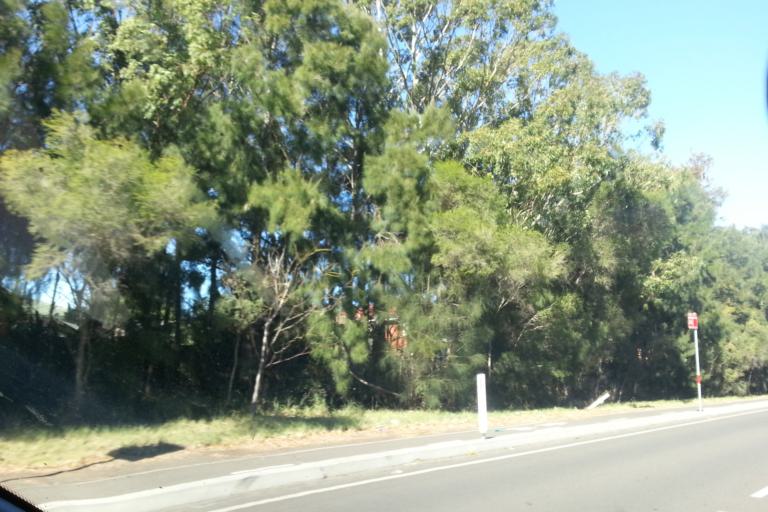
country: AU
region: New South Wales
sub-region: Wollongong
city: Koonawarra
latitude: -34.4878
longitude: 150.7983
